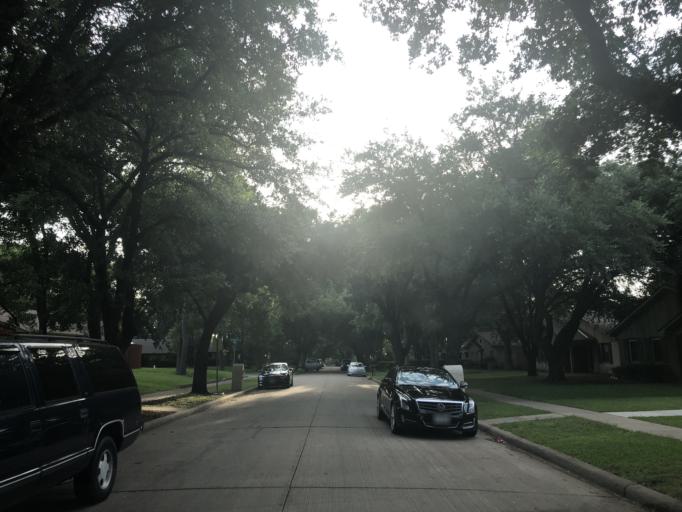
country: US
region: Texas
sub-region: Dallas County
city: Sunnyvale
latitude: 32.8401
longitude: -96.5894
